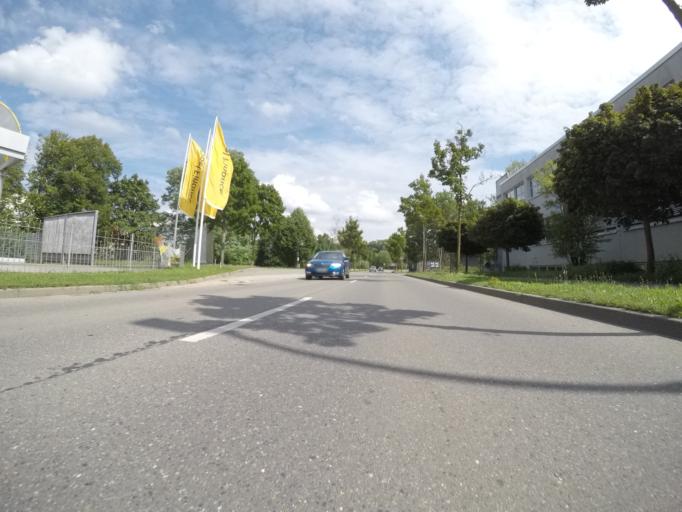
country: DE
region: Baden-Wuerttemberg
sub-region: Tuebingen Region
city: Rottenburg
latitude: 48.4719
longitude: 8.9465
